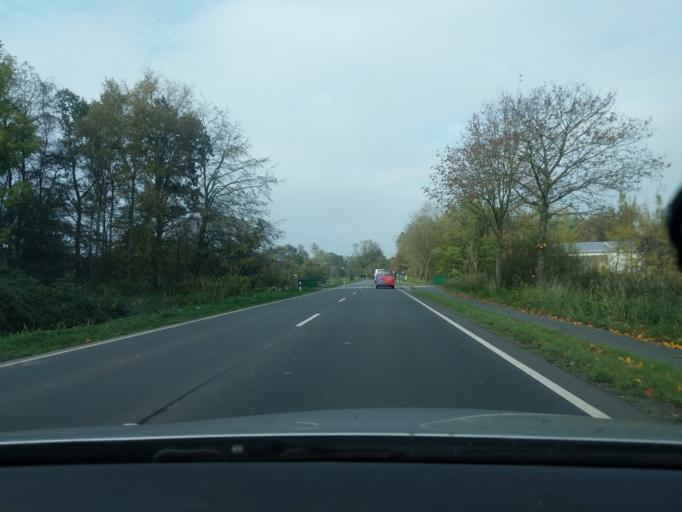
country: DE
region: Lower Saxony
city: Belum
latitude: 53.8123
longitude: 8.9960
